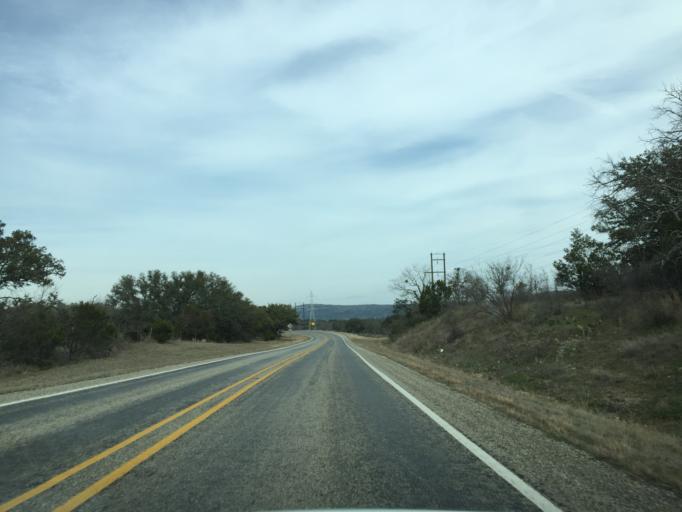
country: US
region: Texas
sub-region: Gillespie County
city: Fredericksburg
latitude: 30.4773
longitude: -98.7078
